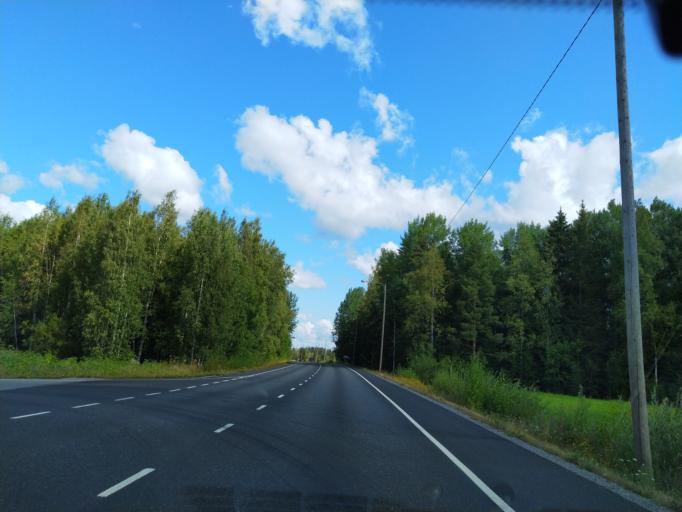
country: FI
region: Satakunta
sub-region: Pori
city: Huittinen
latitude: 61.1753
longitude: 22.7112
